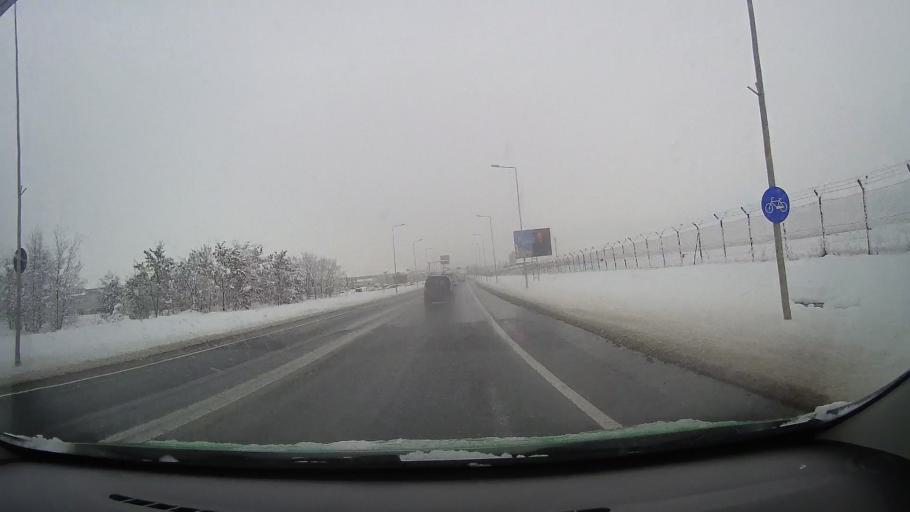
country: RO
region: Sibiu
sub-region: Comuna Sura Mica
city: Sura Mica
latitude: 45.7885
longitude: 24.0811
